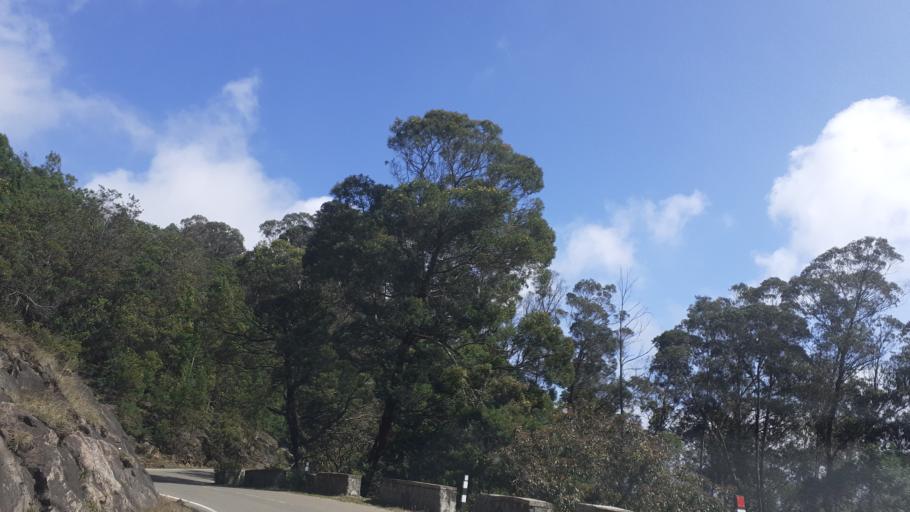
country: IN
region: Tamil Nadu
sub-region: Dindigul
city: Kodaikanal
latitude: 10.2263
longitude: 77.4230
